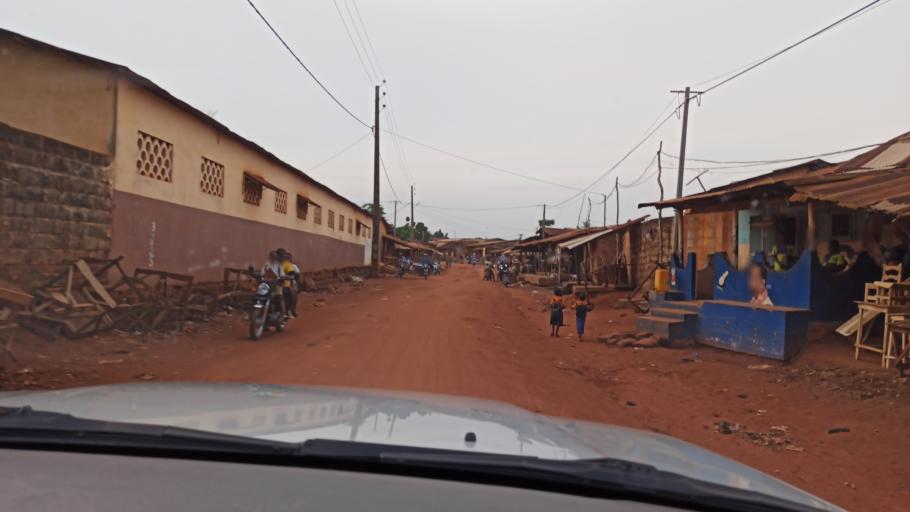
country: BJ
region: Queme
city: Porto-Novo
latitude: 6.5302
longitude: 2.6646
